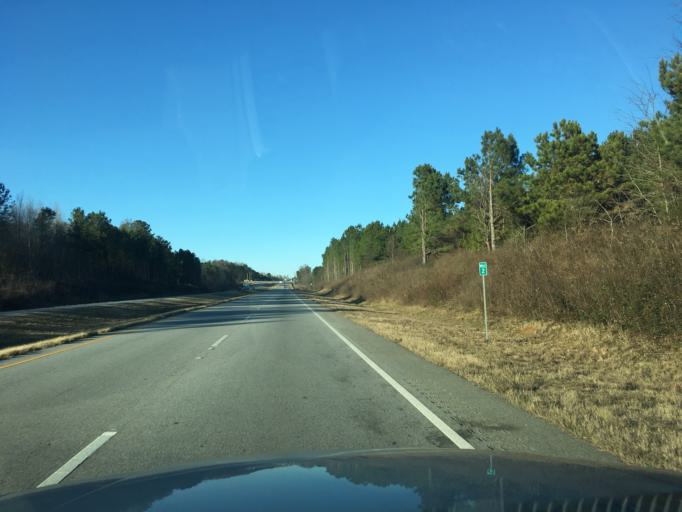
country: US
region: Georgia
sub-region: Carroll County
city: Carrollton
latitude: 33.4535
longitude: -85.1243
